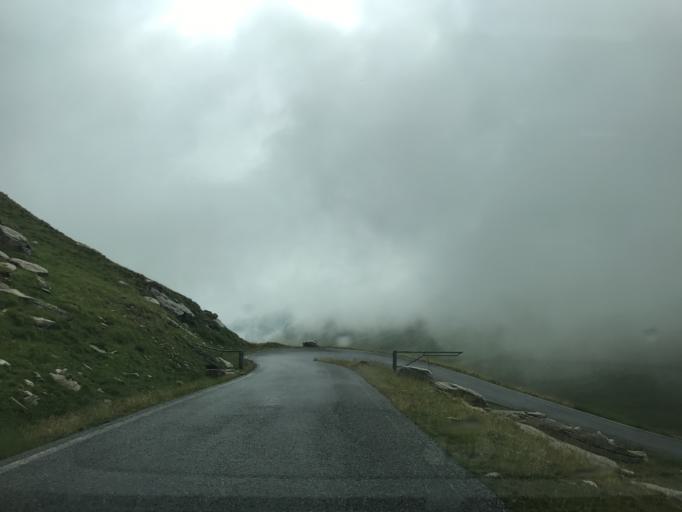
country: IT
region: Piedmont
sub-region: Provincia di Cuneo
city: Pontechianale
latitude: 44.6718
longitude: 6.9882
